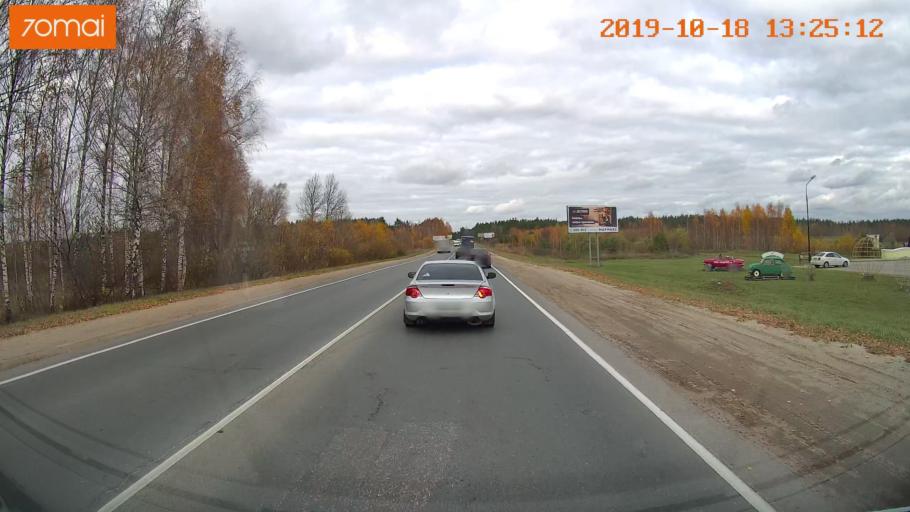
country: RU
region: Rjazan
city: Polyany
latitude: 54.7408
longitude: 39.8410
